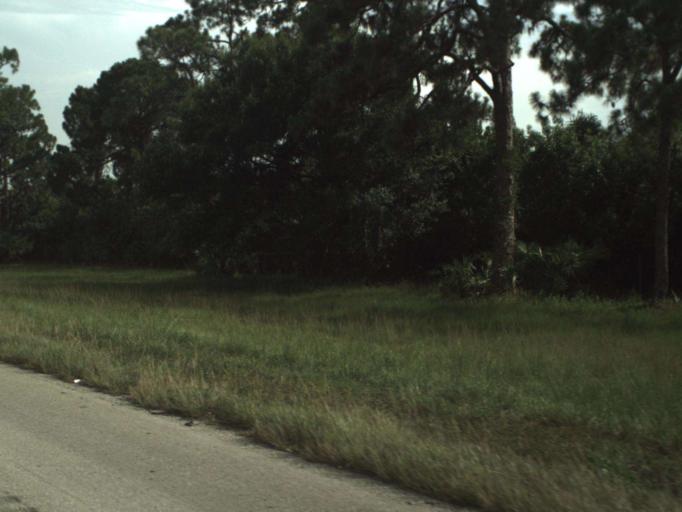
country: US
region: Florida
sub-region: Saint Lucie County
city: Port Saint Lucie
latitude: 27.2483
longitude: -80.4163
